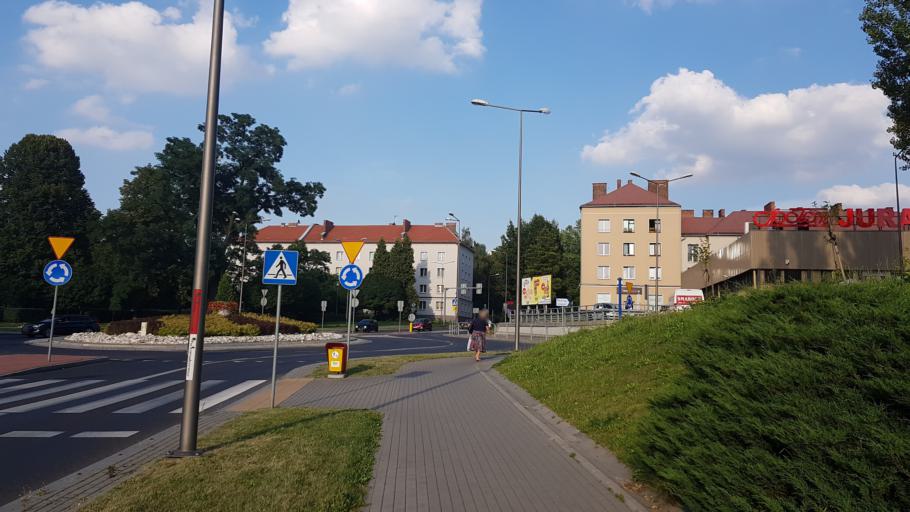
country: PL
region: Silesian Voivodeship
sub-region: Bielsko-Biala
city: Bielsko-Biala
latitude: 49.8155
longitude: 19.0505
